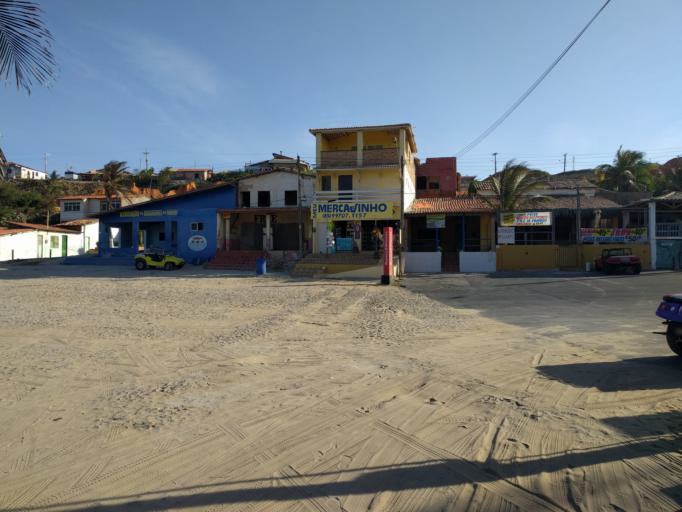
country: BR
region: Ceara
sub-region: Beberibe
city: Beberibe
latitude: -4.1529
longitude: -38.1120
